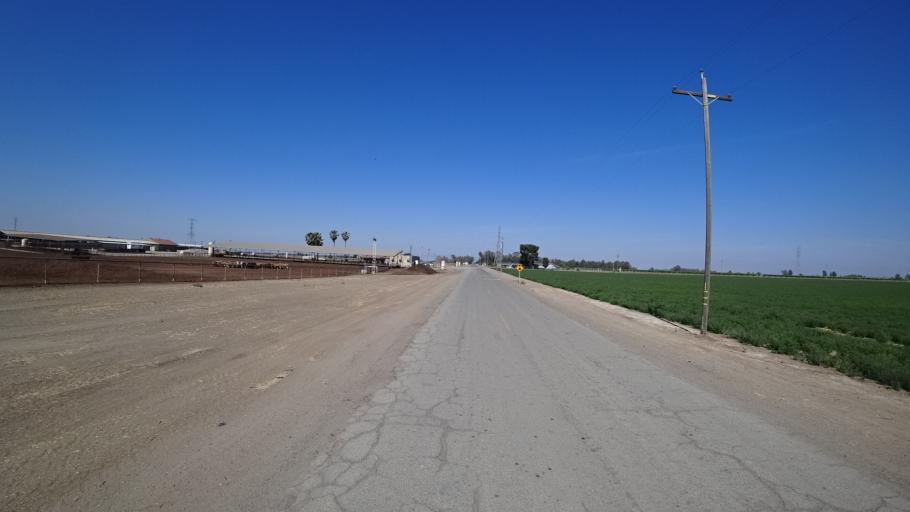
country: US
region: California
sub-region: Fresno County
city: Riverdale
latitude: 36.3512
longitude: -119.8849
